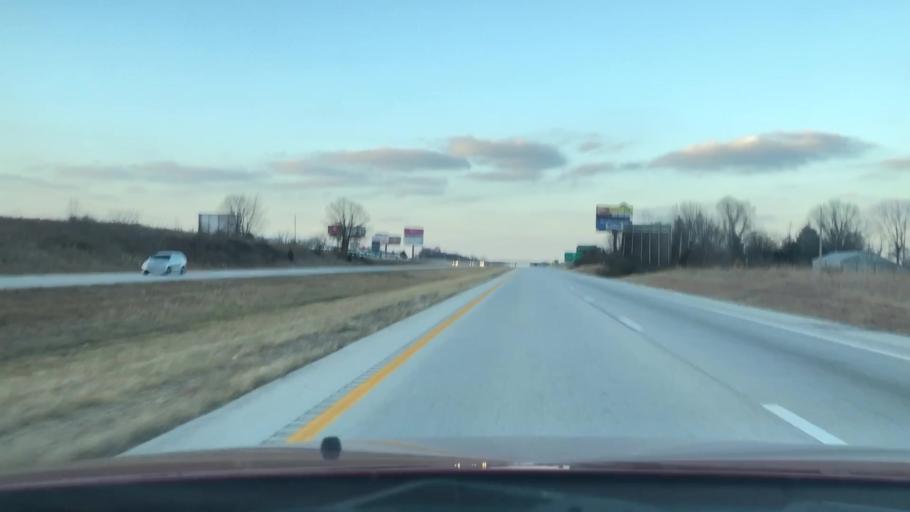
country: US
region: Missouri
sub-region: Christian County
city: Ozark
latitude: 36.9355
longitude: -93.2321
